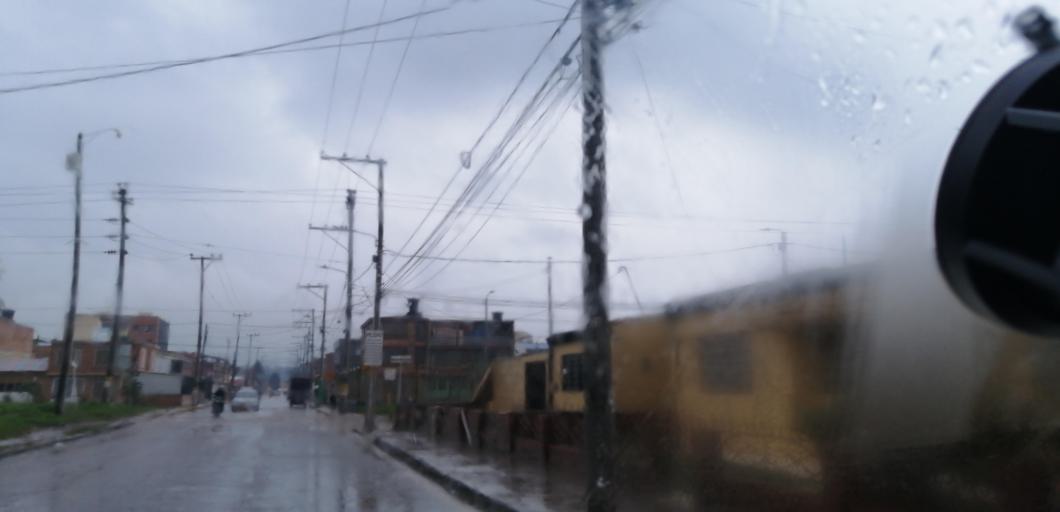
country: CO
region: Cundinamarca
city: Madrid
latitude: 4.7360
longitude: -74.2667
